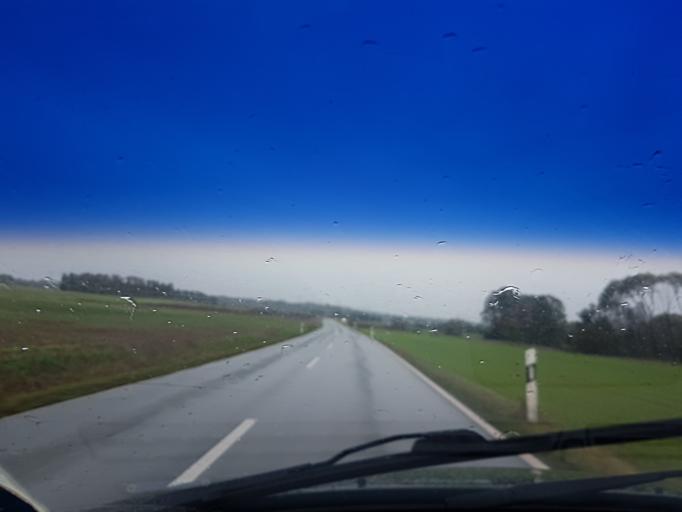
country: DE
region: Bavaria
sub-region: Upper Franconia
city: Schlusselfeld
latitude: 49.7646
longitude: 10.5872
